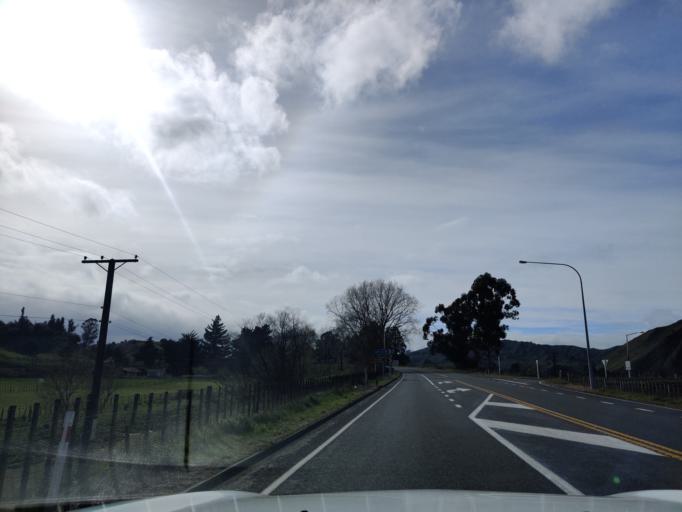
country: NZ
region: Manawatu-Wanganui
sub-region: Ruapehu District
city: Waiouru
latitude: -39.8076
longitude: 175.7935
